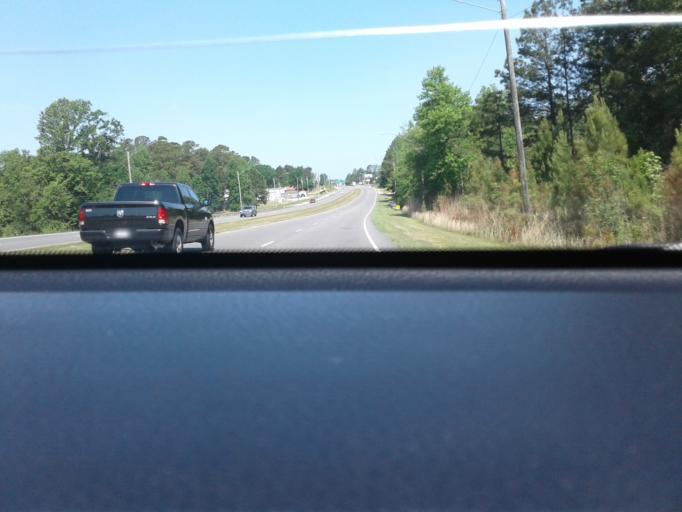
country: US
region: North Carolina
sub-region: Harnett County
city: Lillington
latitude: 35.4123
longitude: -78.7917
